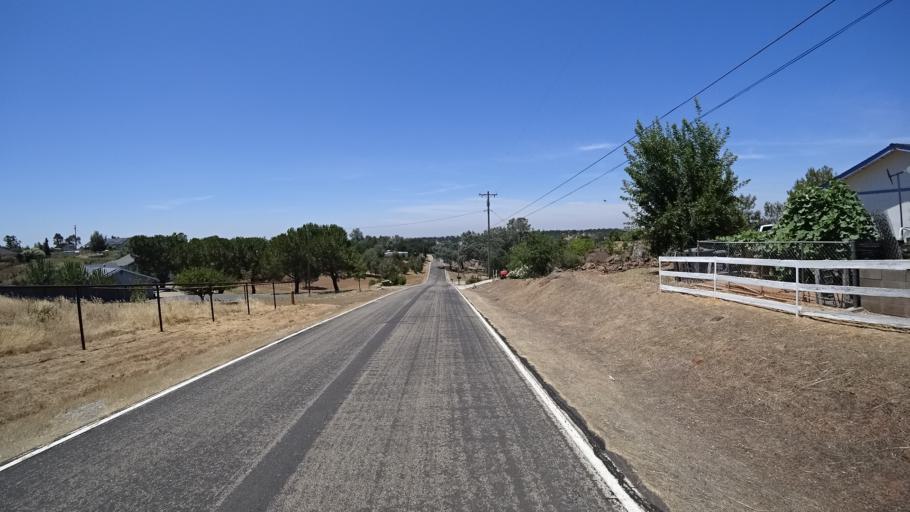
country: US
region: California
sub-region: Calaveras County
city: Rancho Calaveras
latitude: 38.1205
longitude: -120.8507
